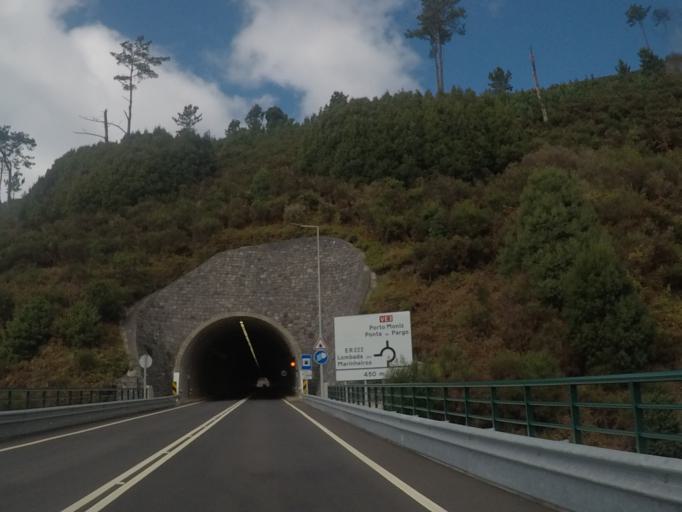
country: PT
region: Madeira
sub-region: Calheta
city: Faja da Ovelha
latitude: 32.7871
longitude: -17.2289
